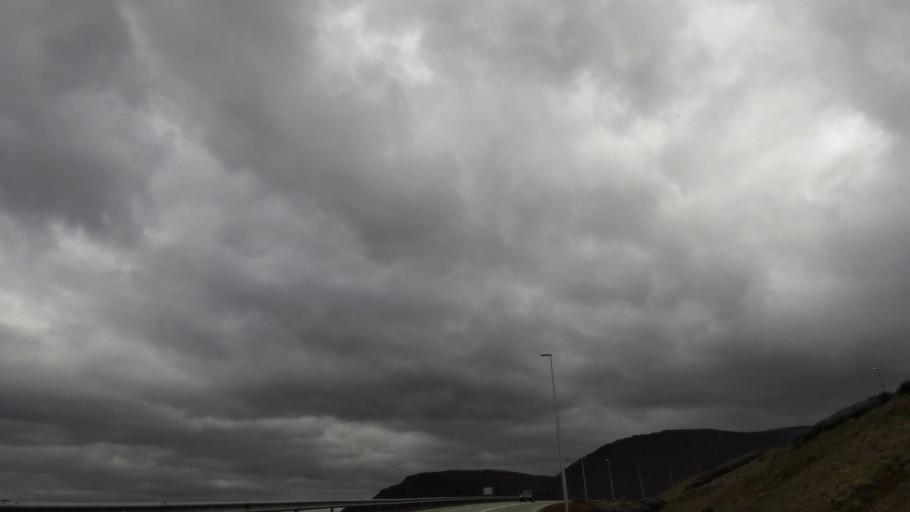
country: IS
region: Westfjords
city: Isafjoerdur
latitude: 66.1081
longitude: -23.1122
